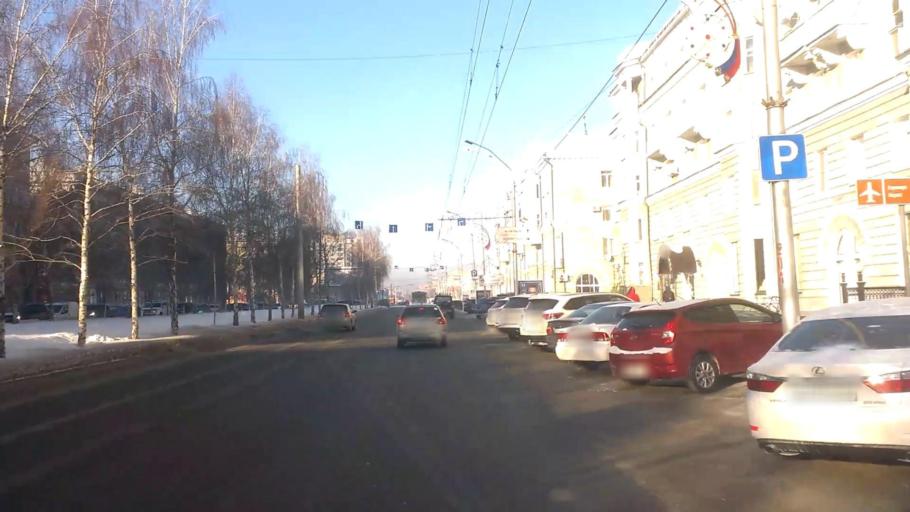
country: RU
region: Altai Krai
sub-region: Gorod Barnaulskiy
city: Barnaul
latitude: 53.3532
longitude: 83.7717
